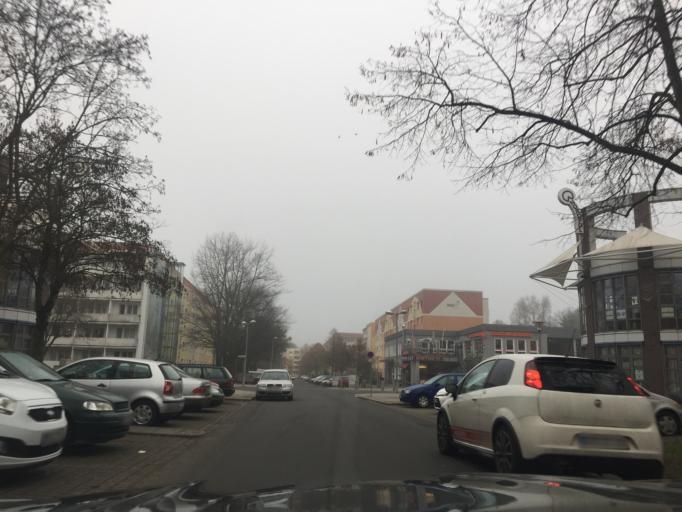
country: DE
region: Brandenburg
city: Hennigsdorf
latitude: 52.6534
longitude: 13.1972
